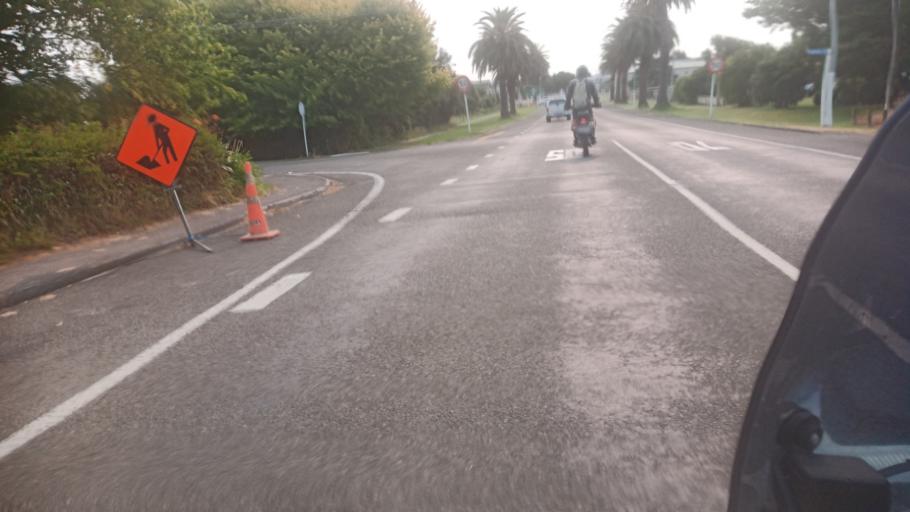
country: NZ
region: Bay of Plenty
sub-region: Opotiki District
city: Opotiki
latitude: -38.0043
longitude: 177.2900
